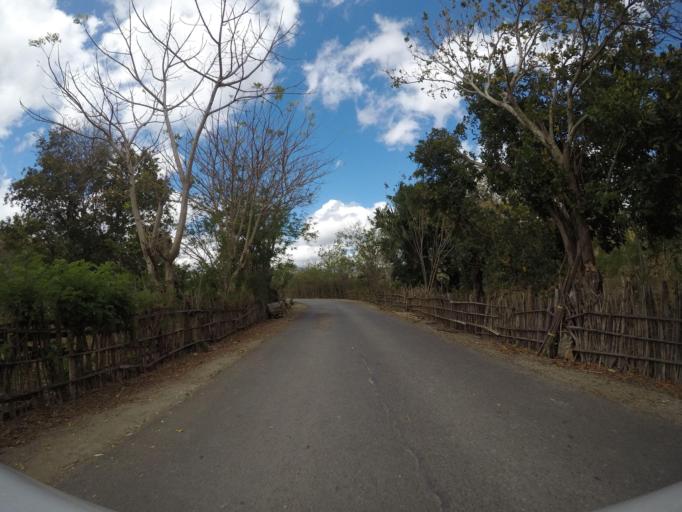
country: TL
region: Lautem
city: Lospalos
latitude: -8.4570
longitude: 126.8213
